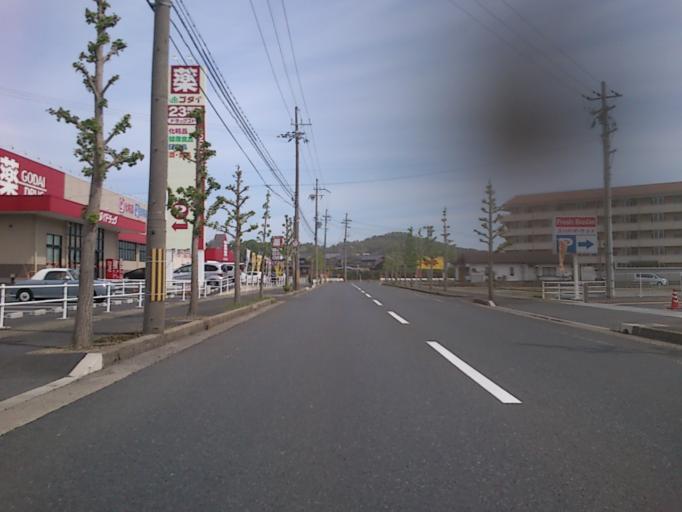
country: JP
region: Kyoto
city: Miyazu
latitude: 35.6790
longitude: 135.0239
